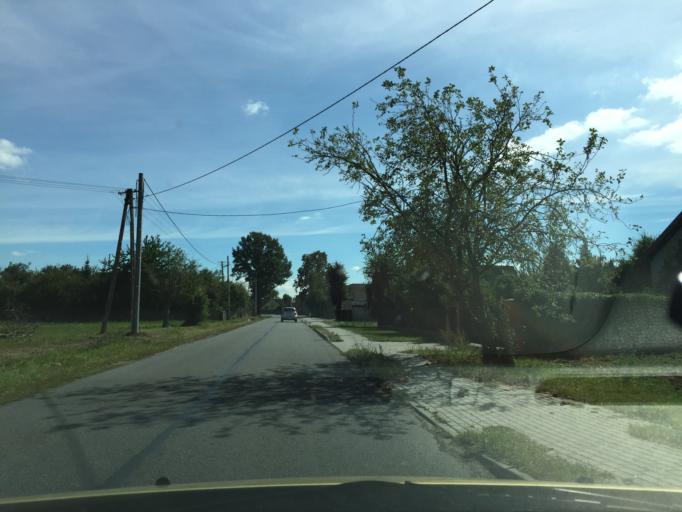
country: PL
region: Greater Poland Voivodeship
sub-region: Powiat kaliski
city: Stawiszyn
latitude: 51.9457
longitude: 18.1838
